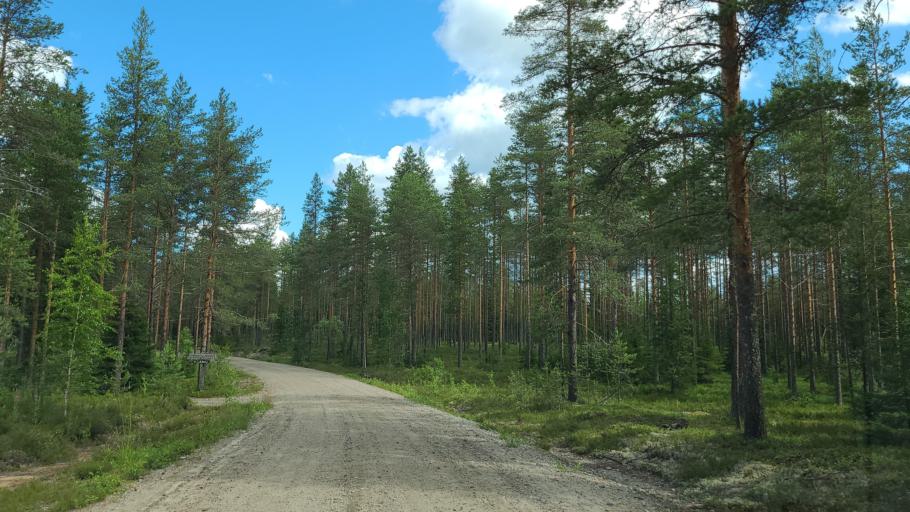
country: FI
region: Northern Savo
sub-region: Koillis-Savo
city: Kaavi
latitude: 63.0589
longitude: 28.8260
